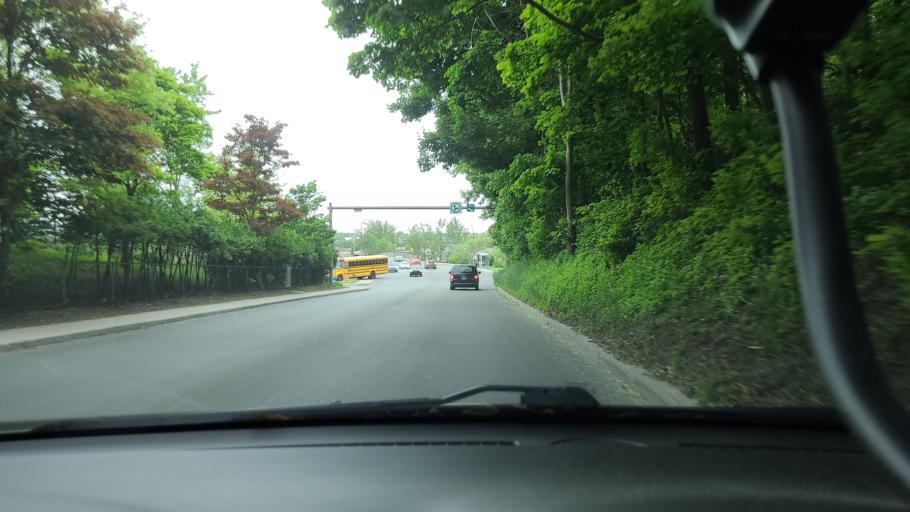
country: CA
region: Quebec
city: Montreal-Ouest
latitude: 45.4496
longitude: -73.6425
